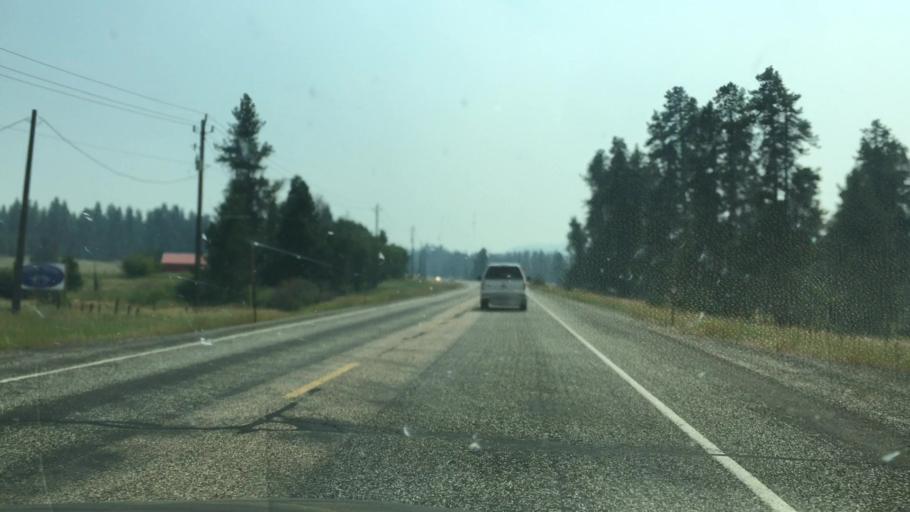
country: US
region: Idaho
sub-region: Valley County
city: Cascade
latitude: 44.3935
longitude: -116.0075
